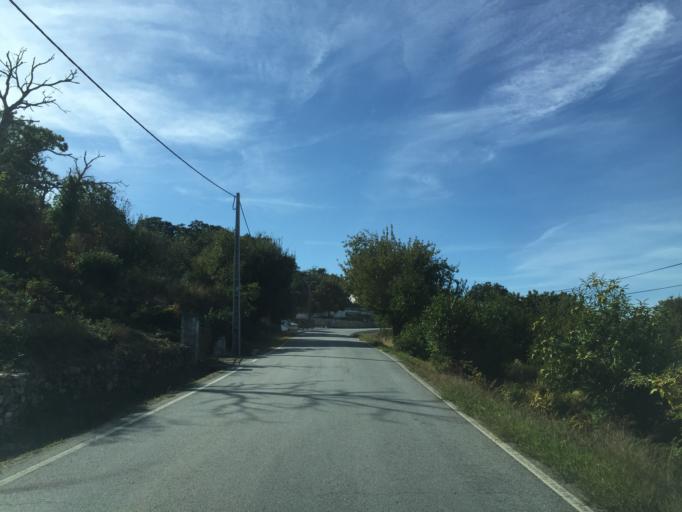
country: PT
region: Portalegre
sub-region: Marvao
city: Marvao
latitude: 39.4018
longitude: -7.3775
